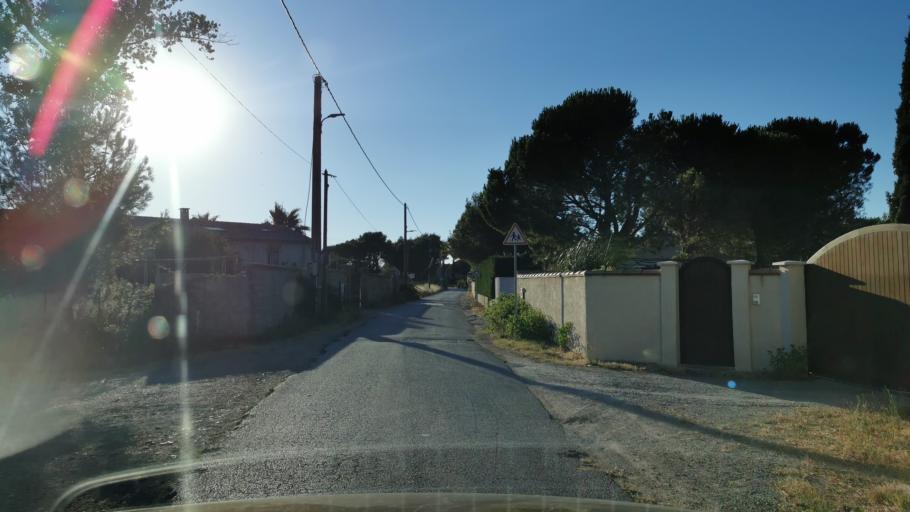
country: FR
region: Languedoc-Roussillon
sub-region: Departement de l'Aude
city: Coursan
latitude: 43.2667
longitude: 3.0181
